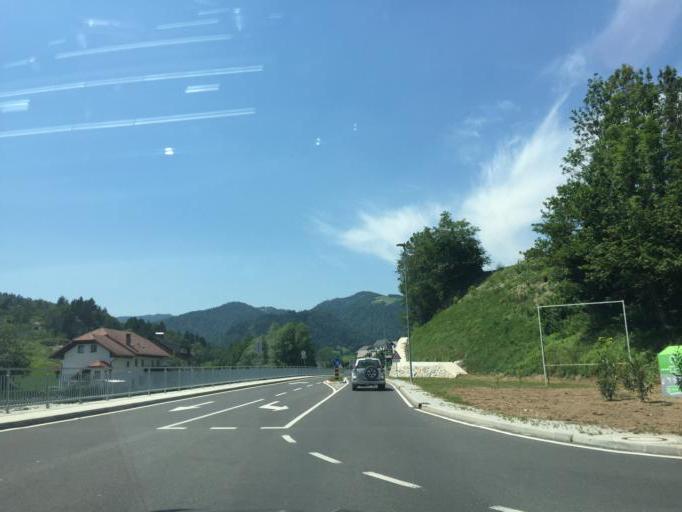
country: SI
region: Gorenja Vas-Poljane
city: Gorenja Vas
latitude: 46.1055
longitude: 14.1373
